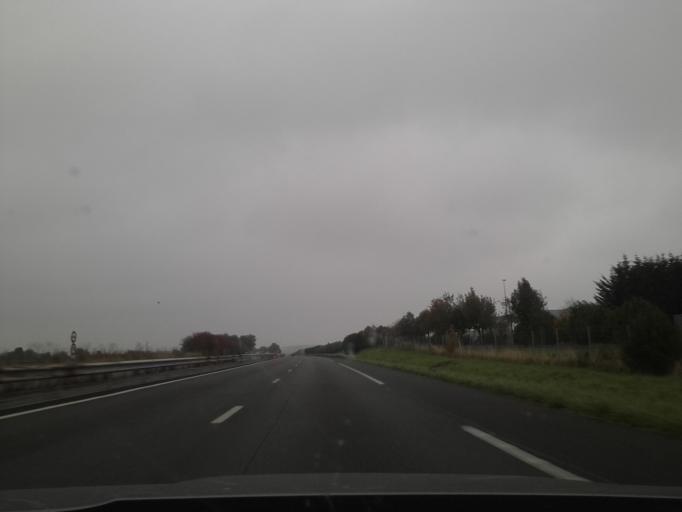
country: FR
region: Nord-Pas-de-Calais
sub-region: Departement du Nord
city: Neuville-Saint-Remy
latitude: 50.1919
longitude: 3.1995
